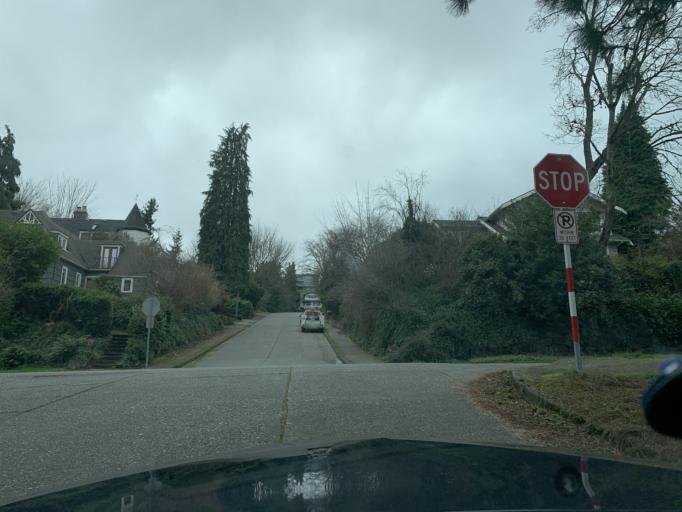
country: US
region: Washington
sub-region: King County
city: Seattle
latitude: 47.5877
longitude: -122.2891
